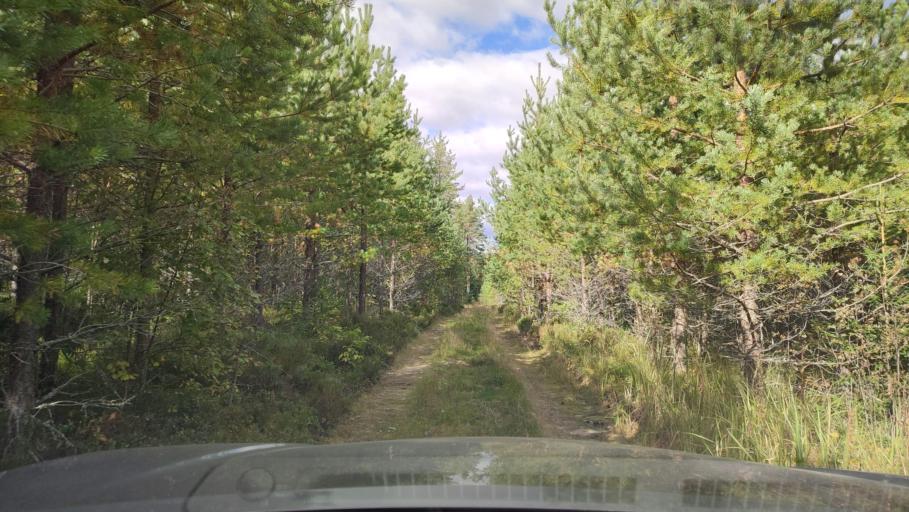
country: FI
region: Southern Ostrobothnia
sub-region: Suupohja
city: Karijoki
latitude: 62.2203
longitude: 21.6208
